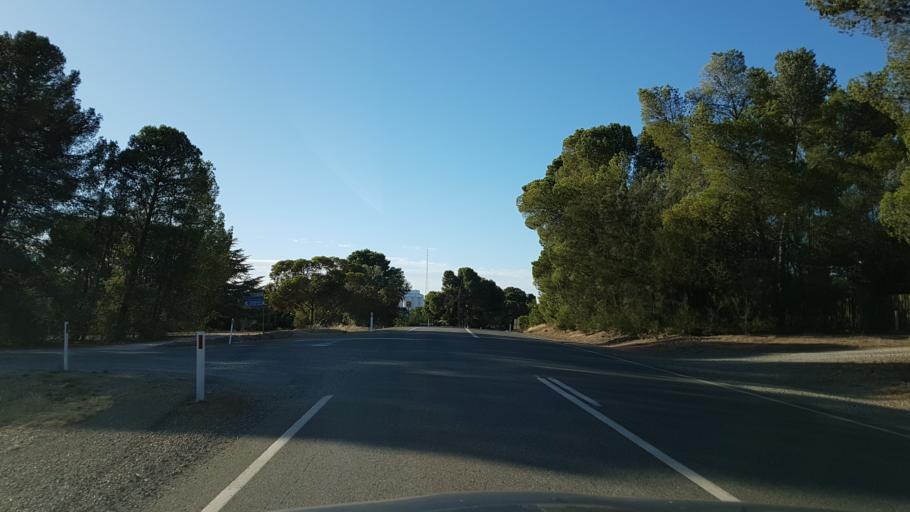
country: AU
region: South Australia
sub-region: Port Pirie City and Dists
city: Crystal Brook
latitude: -33.2694
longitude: 138.3510
